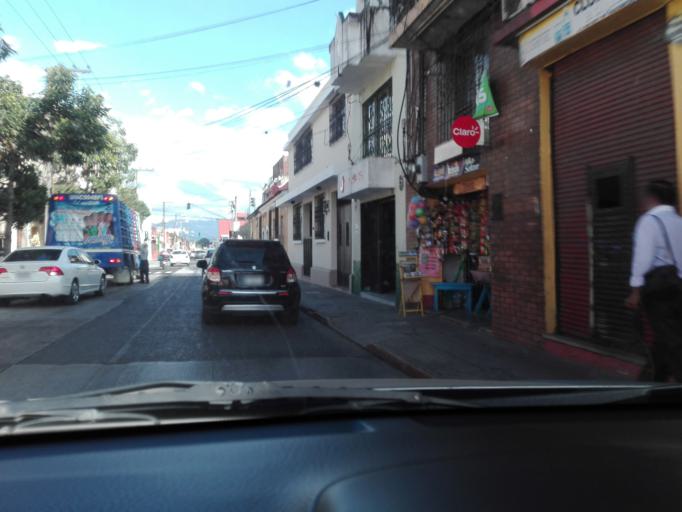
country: GT
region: Guatemala
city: Guatemala City
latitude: 14.6456
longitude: -90.5117
